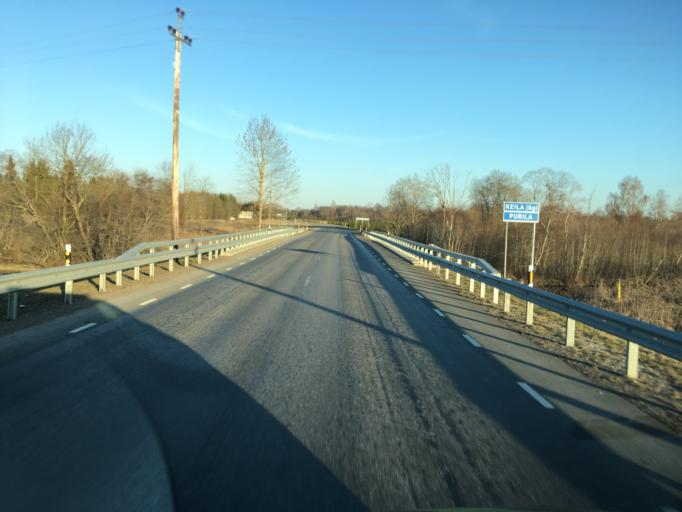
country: EE
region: Raplamaa
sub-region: Rapla vald
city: Rapla
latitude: 59.0813
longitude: 24.8278
